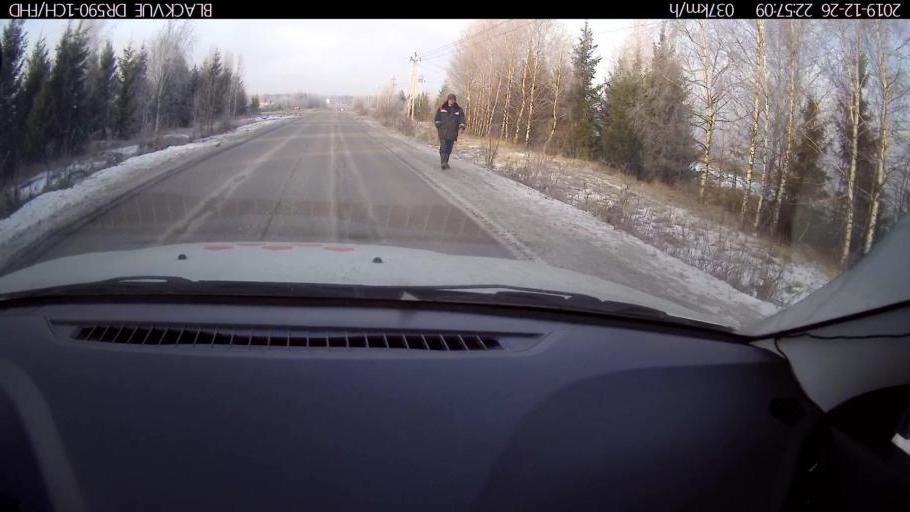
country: RU
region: Nizjnij Novgorod
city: Burevestnik
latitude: 56.1492
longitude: 43.7179
